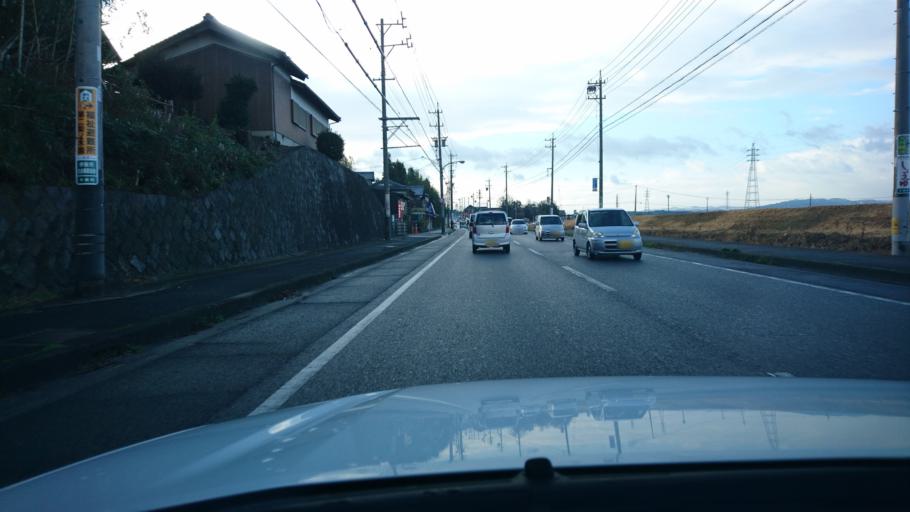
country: JP
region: Mie
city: Ueno-ebisumachi
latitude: 34.7612
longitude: 136.1237
